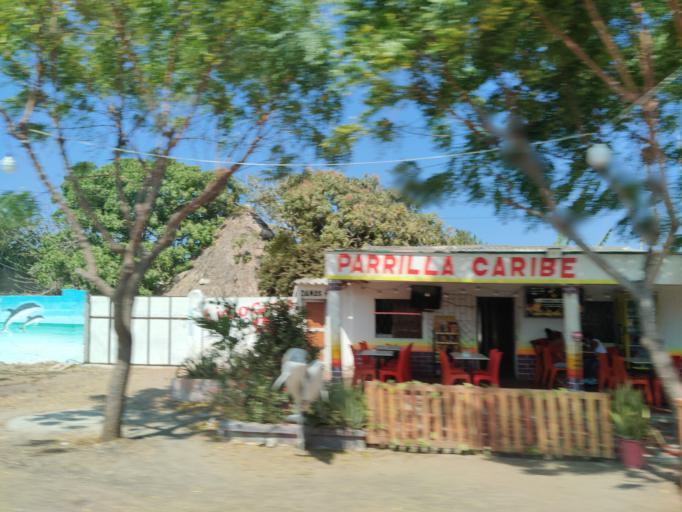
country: CO
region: Bolivar
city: Santa Catalina
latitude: 10.7331
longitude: -75.2638
